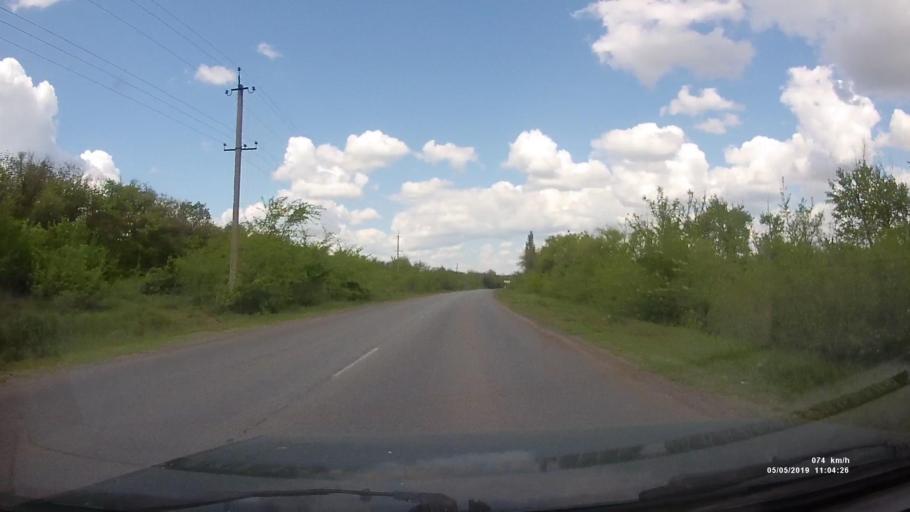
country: RU
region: Rostov
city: Ust'-Donetskiy
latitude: 47.6972
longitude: 40.9182
